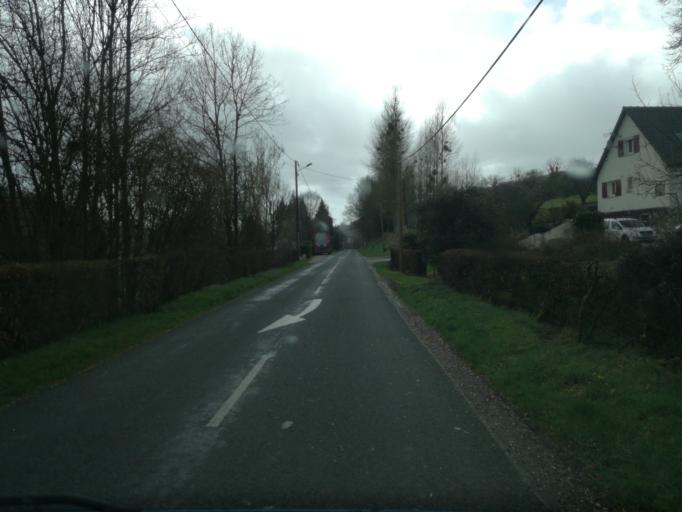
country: FR
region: Haute-Normandie
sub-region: Departement de la Seine-Maritime
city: Saint-Wandrille-Rancon
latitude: 49.5436
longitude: 0.7557
